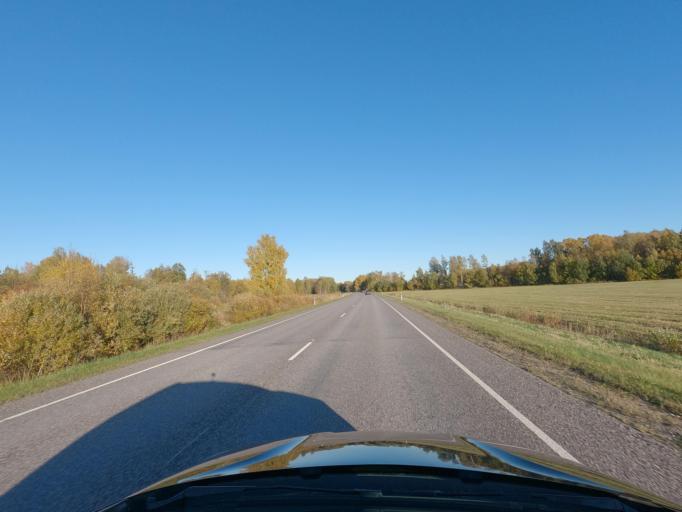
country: EE
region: Saare
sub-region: Orissaare vald
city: Orissaare
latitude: 58.5259
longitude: 23.0537
